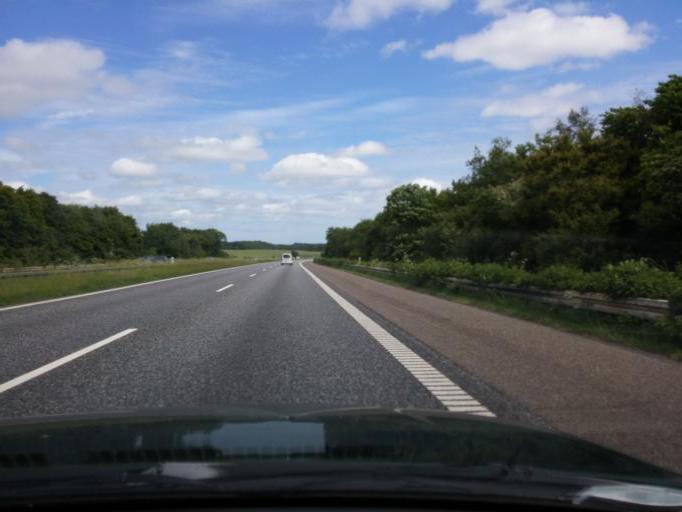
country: DK
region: South Denmark
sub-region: Fredericia Kommune
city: Taulov
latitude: 55.5462
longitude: 9.5641
